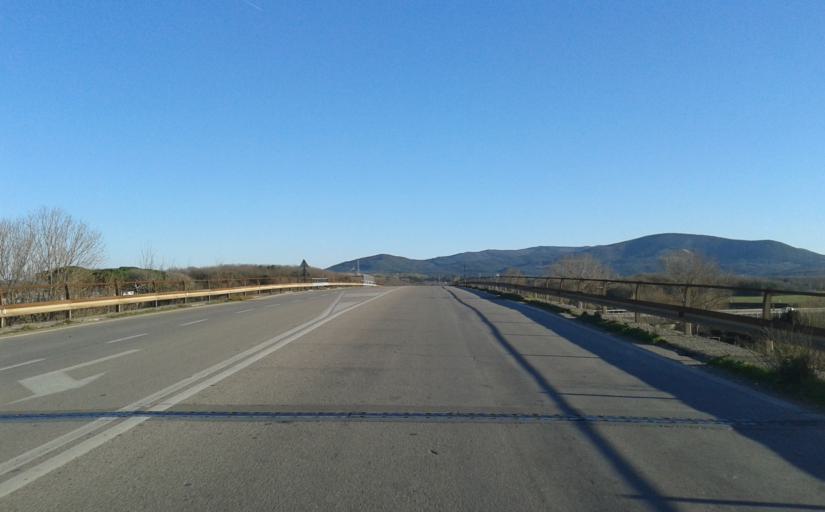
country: IT
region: Tuscany
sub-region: Provincia di Livorno
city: Livorno
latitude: 43.5742
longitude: 10.3463
